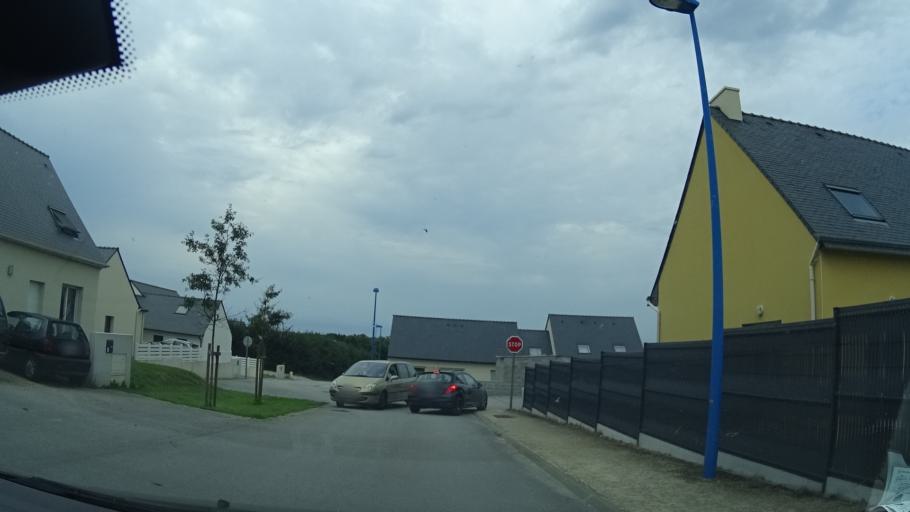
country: FR
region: Brittany
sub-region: Departement du Finistere
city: Plouarzel
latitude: 48.4355
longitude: -4.7323
